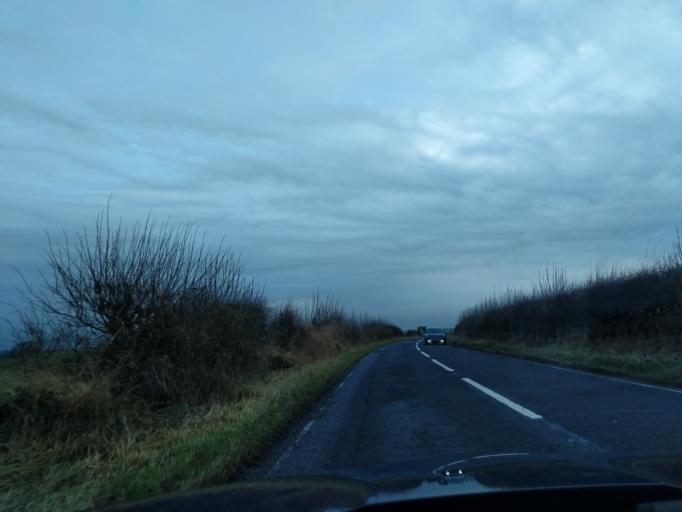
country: GB
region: England
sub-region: Northumberland
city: Rothley
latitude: 55.1335
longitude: -1.9623
